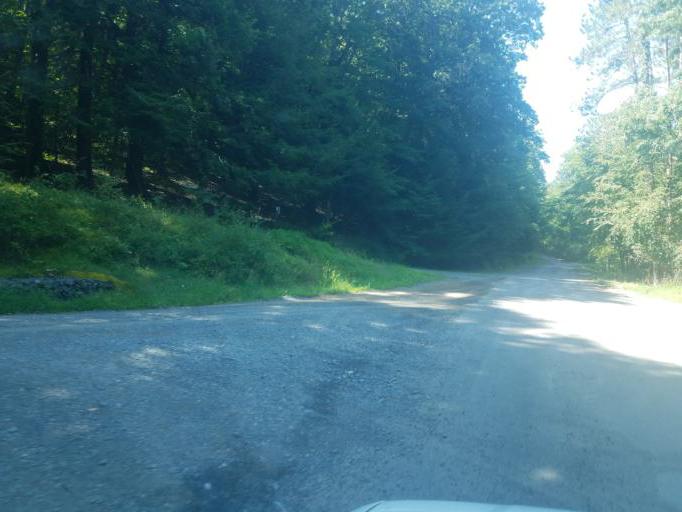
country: US
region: Pennsylvania
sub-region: Clarion County
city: Marianne
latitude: 41.1920
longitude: -79.4389
